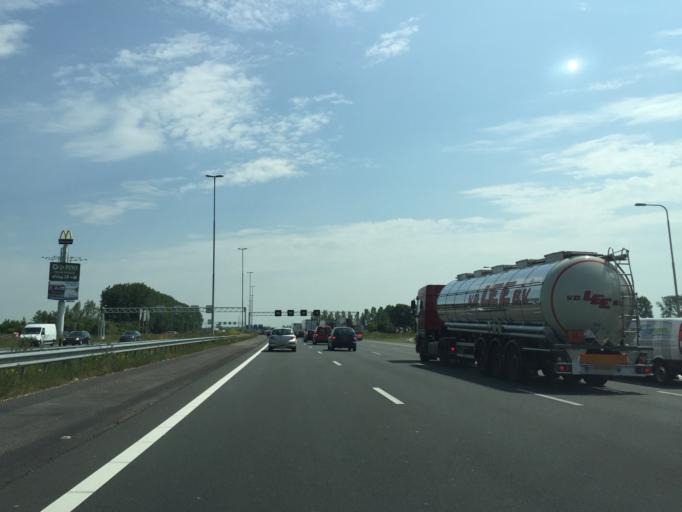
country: NL
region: Gelderland
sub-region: Gemeente Zaltbommel
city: Zaltbommel
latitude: 51.8778
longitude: 5.2092
